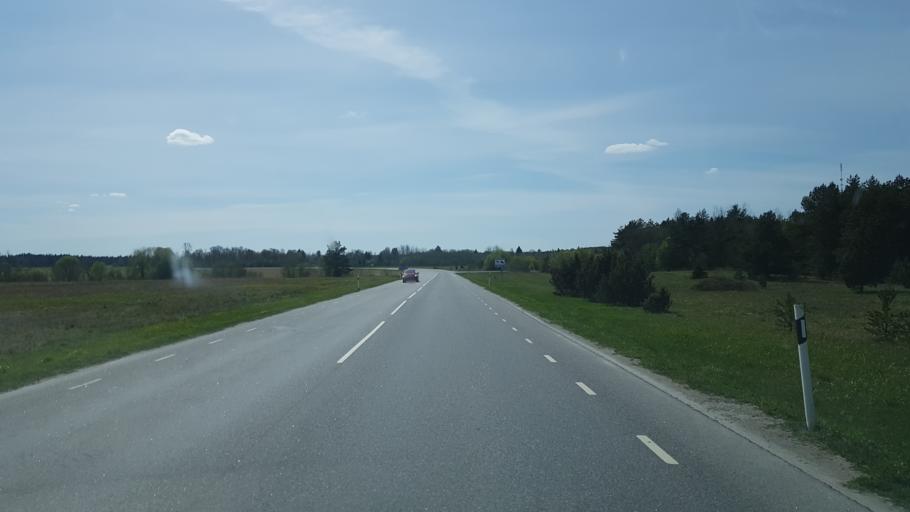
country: EE
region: Harju
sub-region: Paldiski linn
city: Paldiski
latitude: 59.2182
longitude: 24.1000
